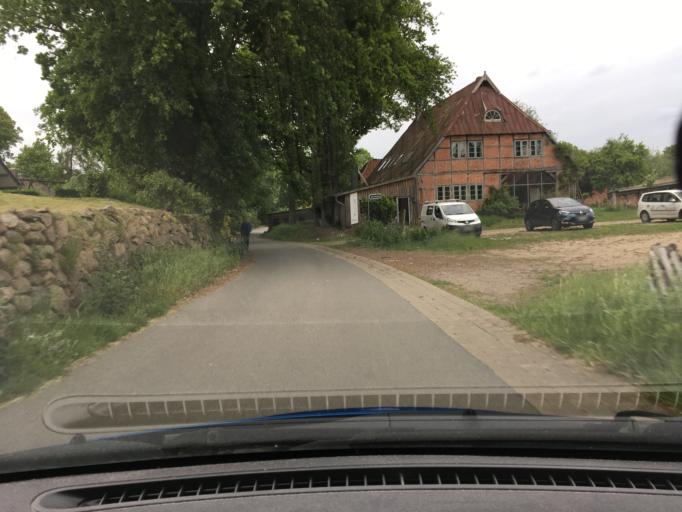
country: DE
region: Lower Saxony
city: Eyendorf
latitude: 53.1999
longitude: 10.1496
